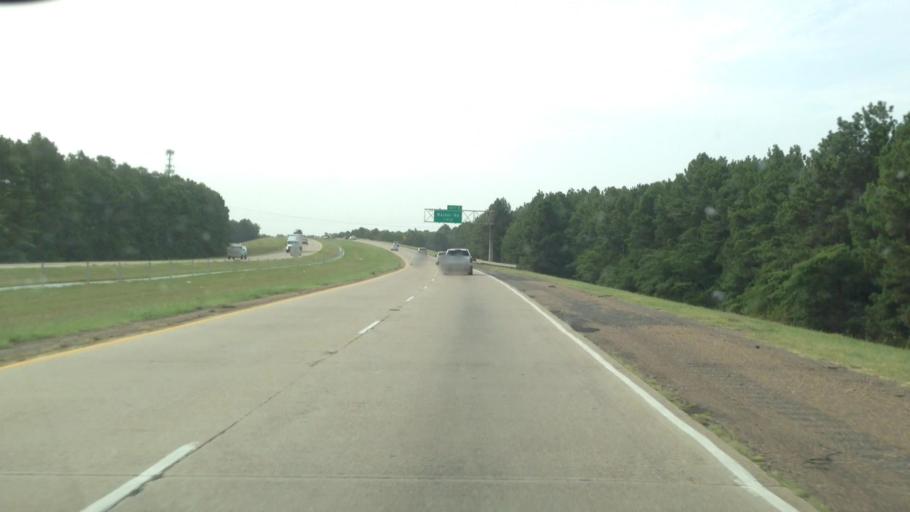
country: US
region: Louisiana
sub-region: Caddo Parish
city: Shreveport
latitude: 32.4225
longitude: -93.8354
